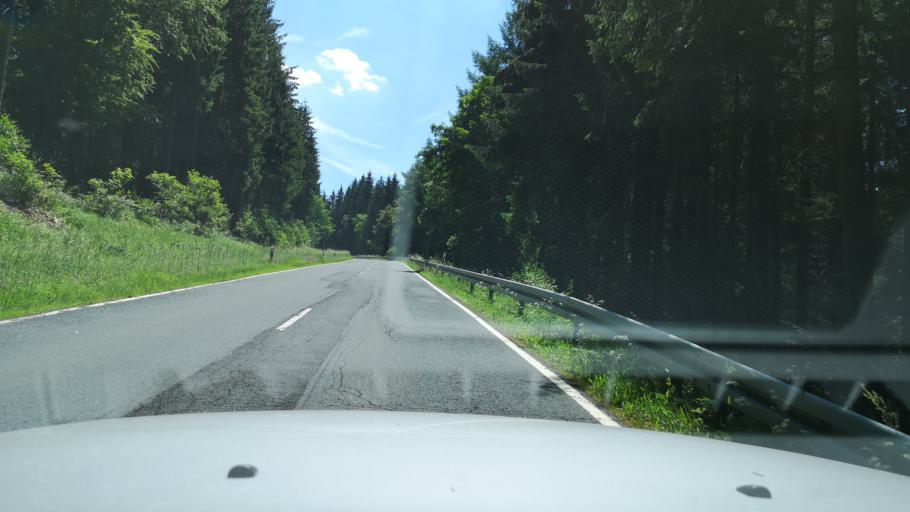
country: DE
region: Bavaria
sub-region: Upper Franconia
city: Tschirn
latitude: 50.4058
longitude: 11.4681
